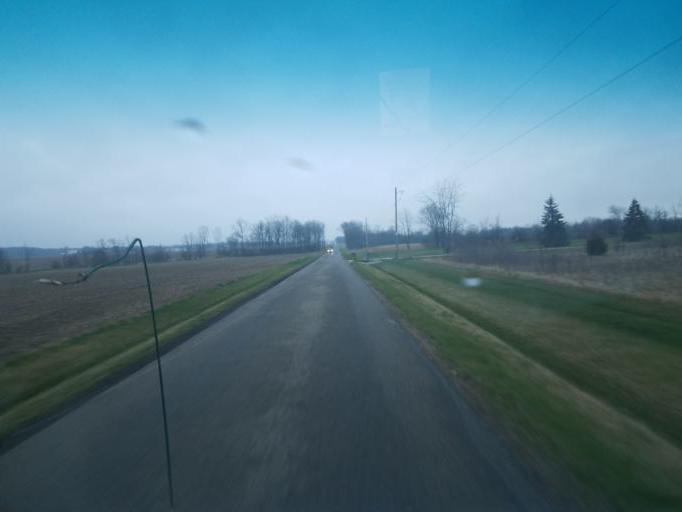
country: US
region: Ohio
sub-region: Defiance County
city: Hicksville
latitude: 41.3391
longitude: -84.7588
